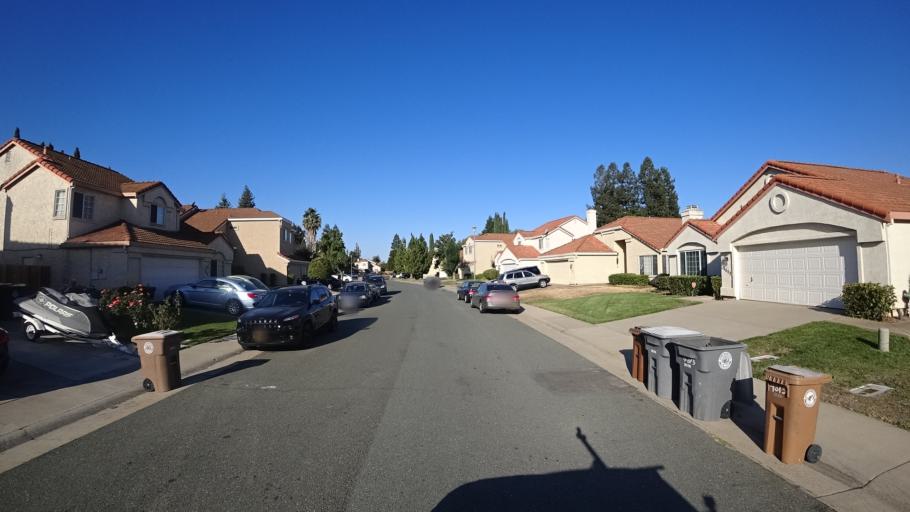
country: US
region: California
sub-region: Sacramento County
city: Laguna
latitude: 38.4323
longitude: -121.4484
